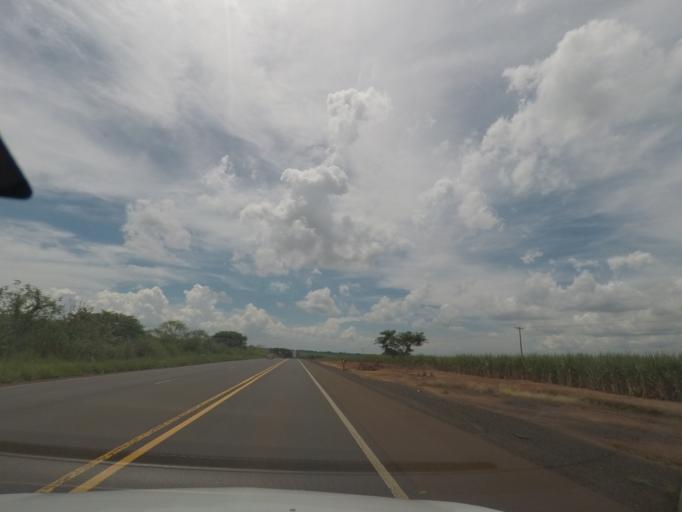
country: BR
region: Sao Paulo
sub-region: Barretos
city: Barretos
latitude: -20.3811
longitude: -48.6424
